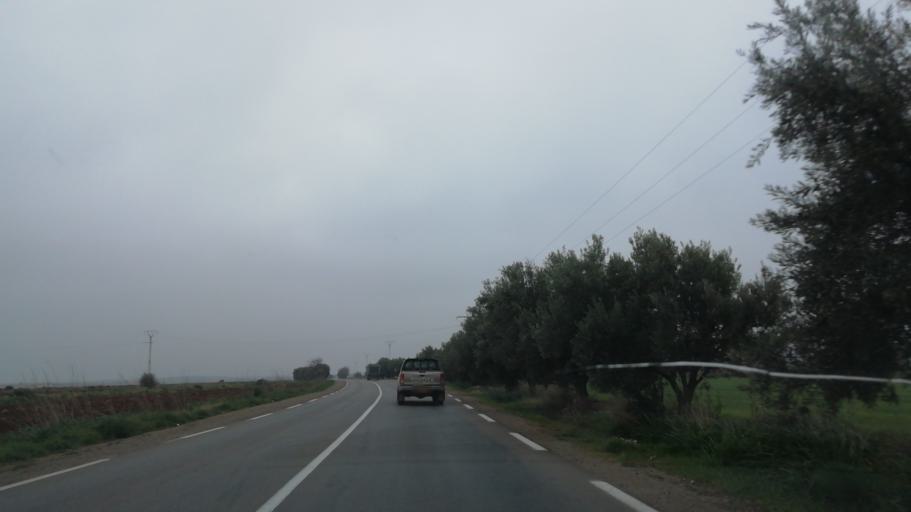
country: DZ
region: Mascara
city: Mascara
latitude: 35.3135
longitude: 0.3860
